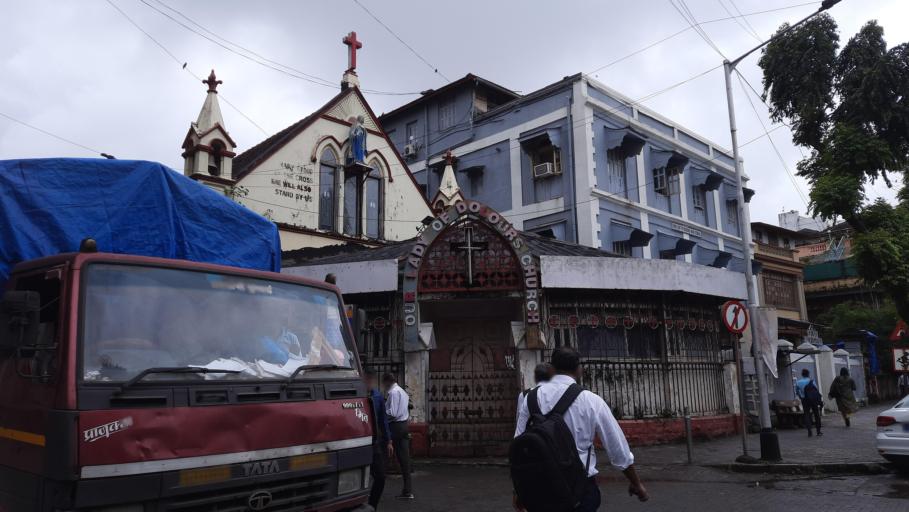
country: IN
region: Maharashtra
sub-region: Raigarh
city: Uran
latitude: 18.9440
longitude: 72.8254
